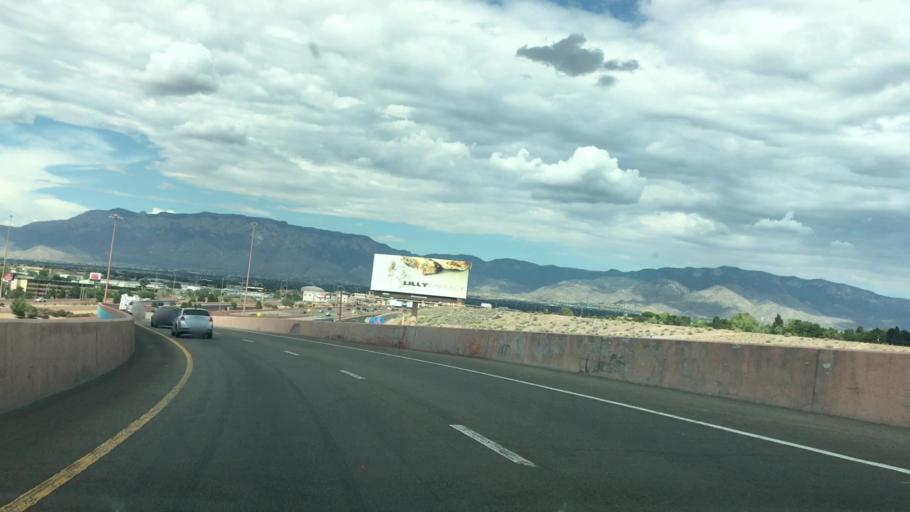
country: US
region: New Mexico
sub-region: Bernalillo County
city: Albuquerque
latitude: 35.1039
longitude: -106.6277
